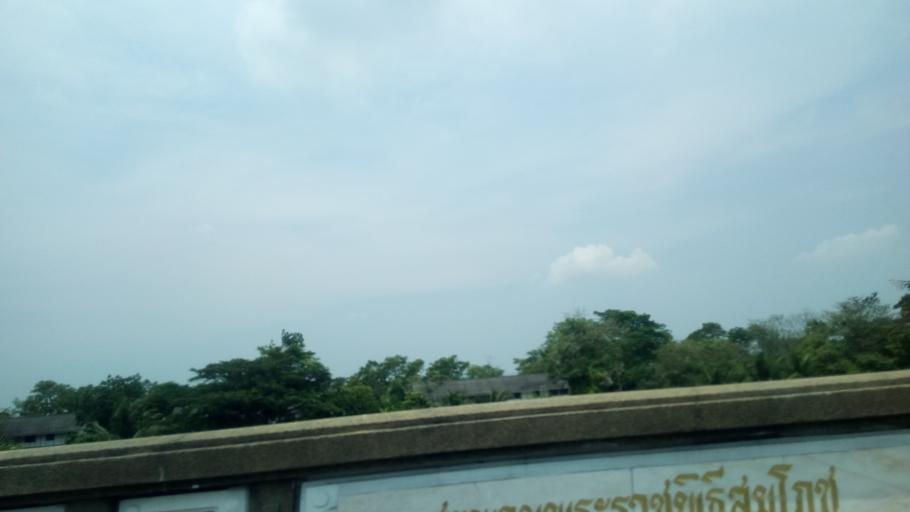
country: TH
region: Bangkok
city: Thawi Watthana
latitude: 13.7754
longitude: 100.3110
